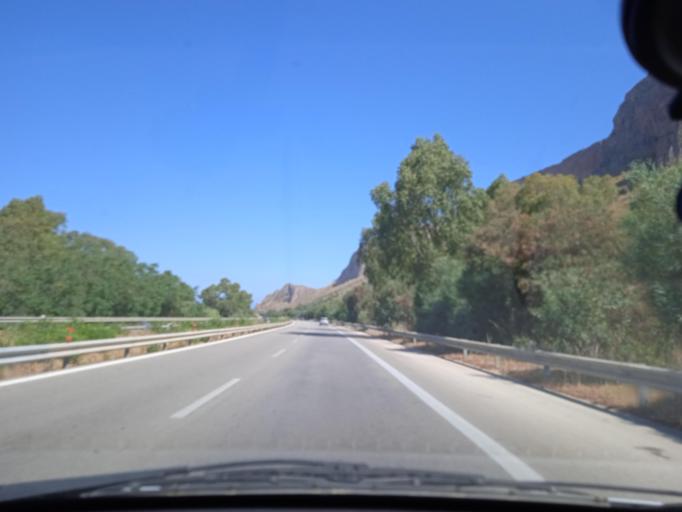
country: IT
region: Sicily
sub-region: Palermo
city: Agliandroni-Paternella
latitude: 38.1103
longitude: 13.0893
